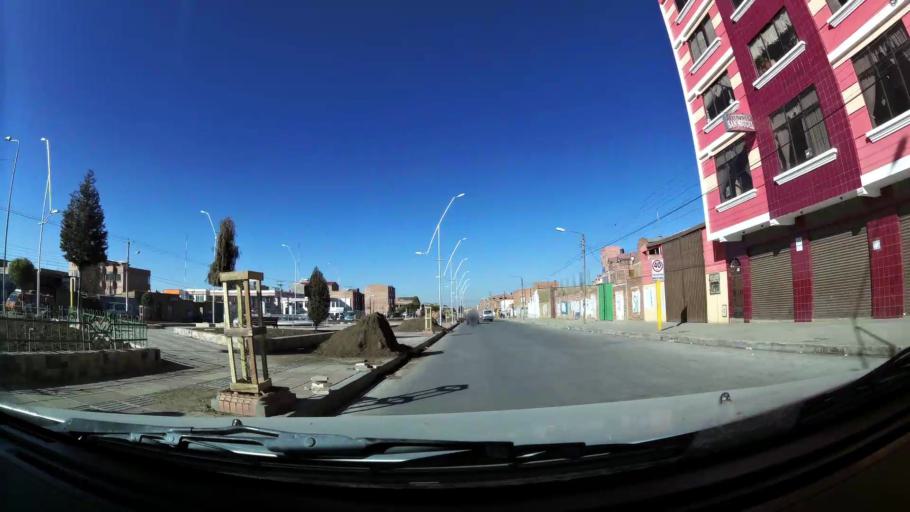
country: BO
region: La Paz
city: La Paz
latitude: -16.5220
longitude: -68.1579
